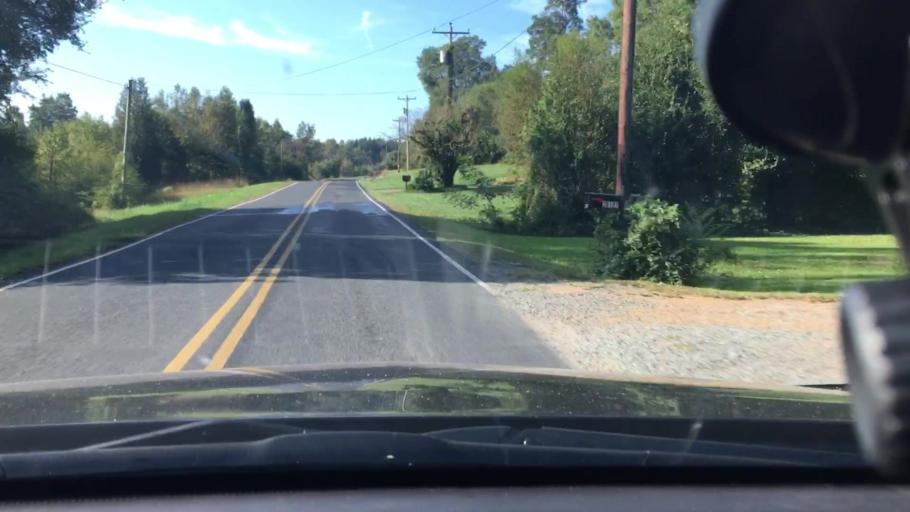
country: US
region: North Carolina
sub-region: Stanly County
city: Badin
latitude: 35.3431
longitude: -80.1240
